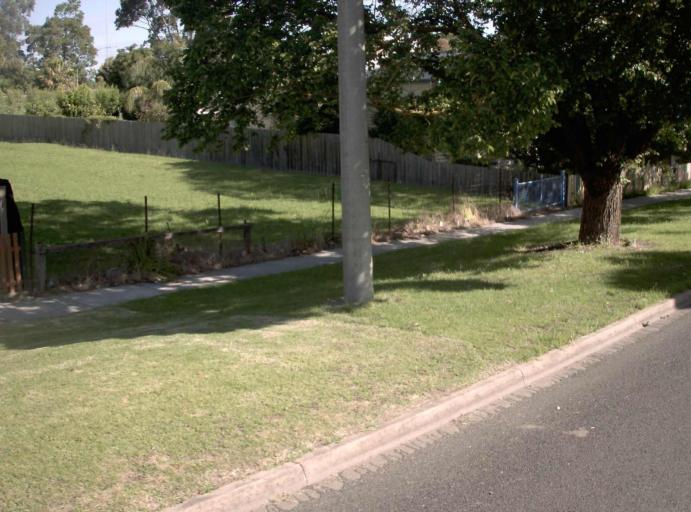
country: AU
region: Victoria
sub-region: East Gippsland
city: Lakes Entrance
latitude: -37.7096
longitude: 148.4537
